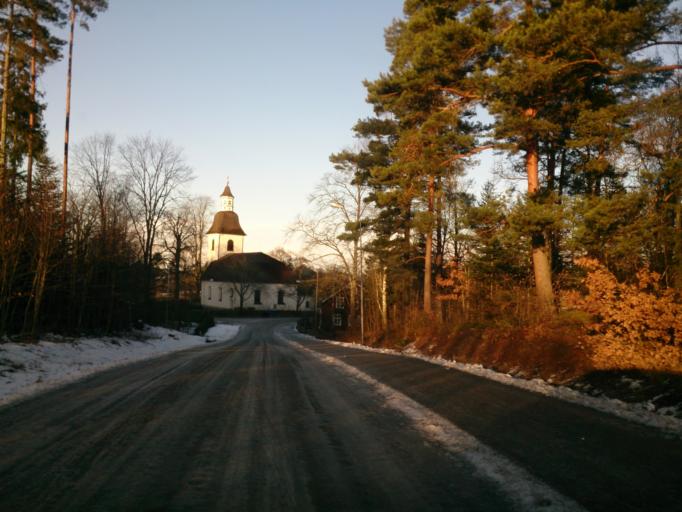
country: SE
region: OEstergoetland
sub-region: Linkopings Kommun
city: Sturefors
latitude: 58.2975
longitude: 15.8669
